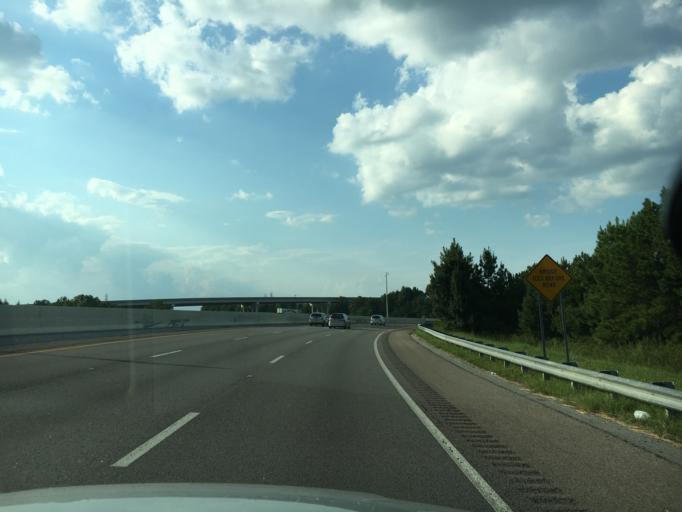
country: US
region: South Carolina
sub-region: Greenville County
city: Simpsonville
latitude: 34.7526
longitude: -82.2857
